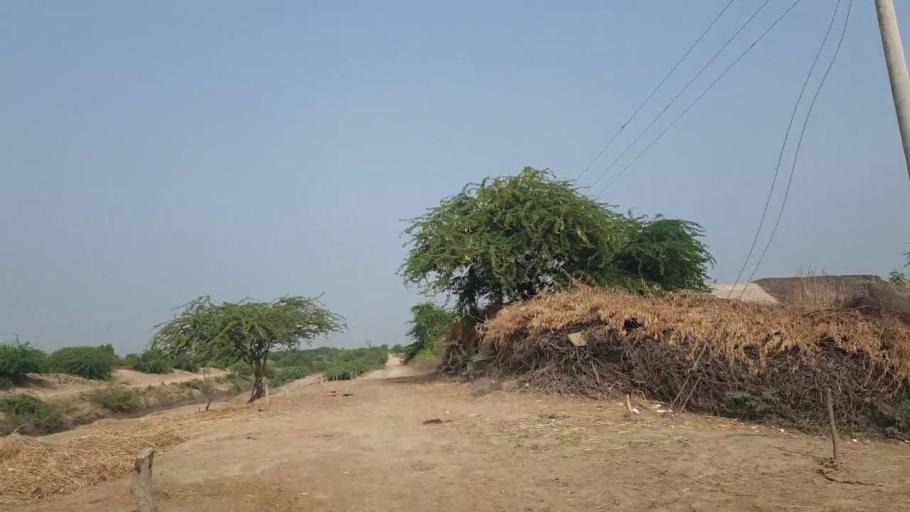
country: PK
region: Sindh
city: Badin
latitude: 24.6949
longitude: 68.7789
